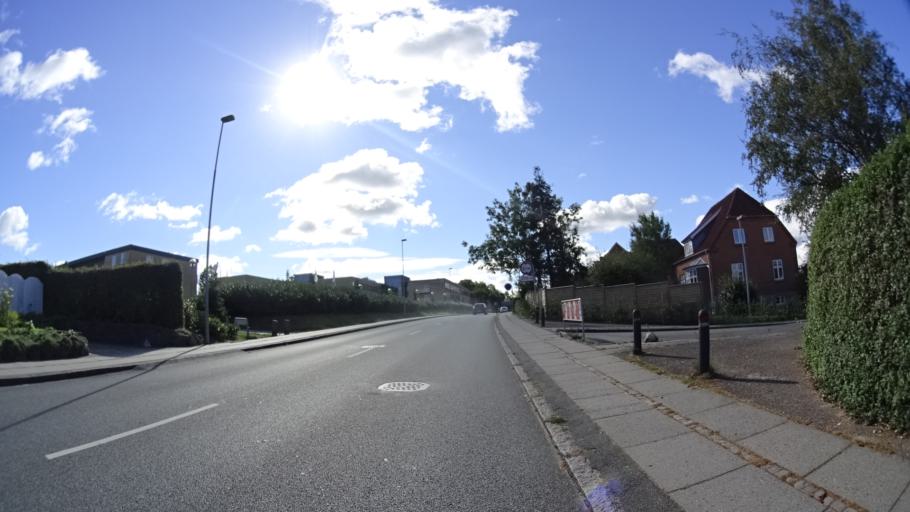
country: DK
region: Central Jutland
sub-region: Arhus Kommune
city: Stavtrup
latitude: 56.1253
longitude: 10.1624
